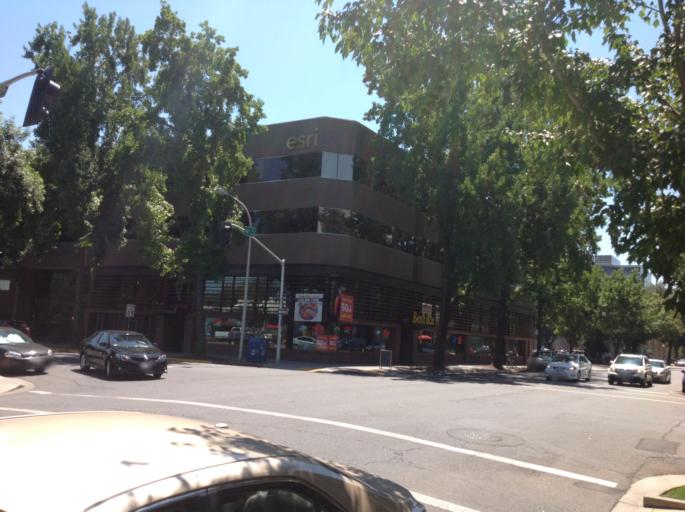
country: US
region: California
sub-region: Sacramento County
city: Sacramento
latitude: 38.5773
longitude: -121.4860
